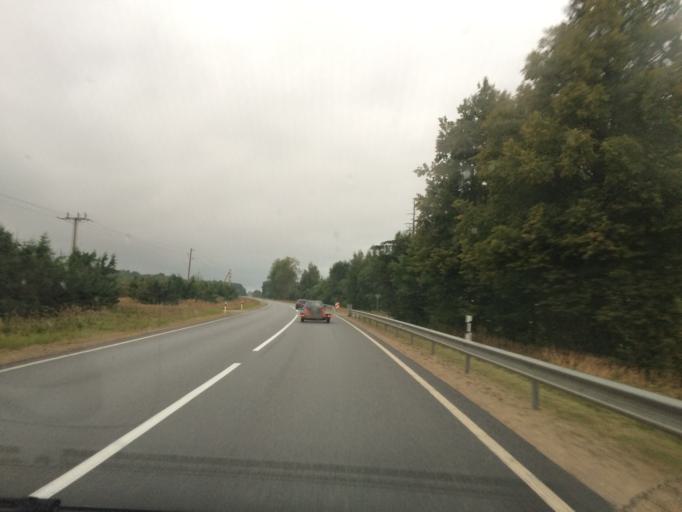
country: LV
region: Livani
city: Livani
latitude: 56.5350
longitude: 26.3082
